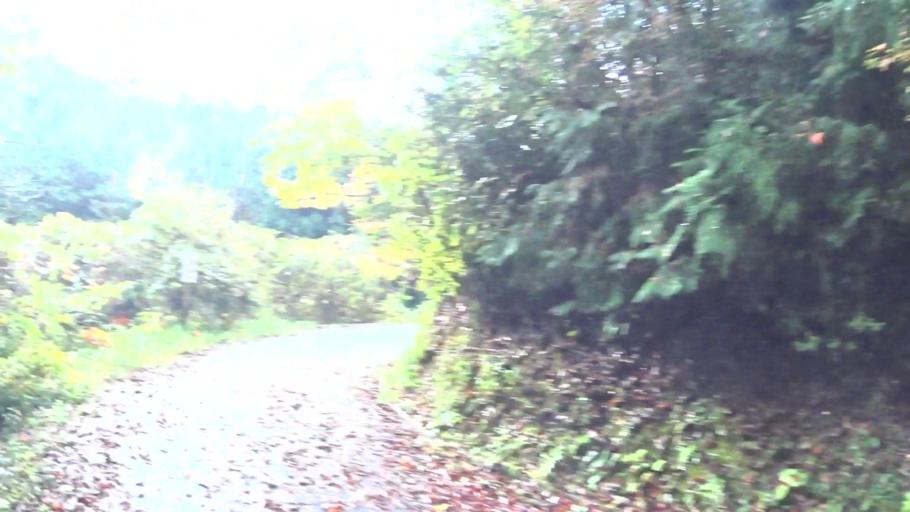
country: JP
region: Kyoto
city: Ayabe
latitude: 35.2635
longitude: 135.2257
